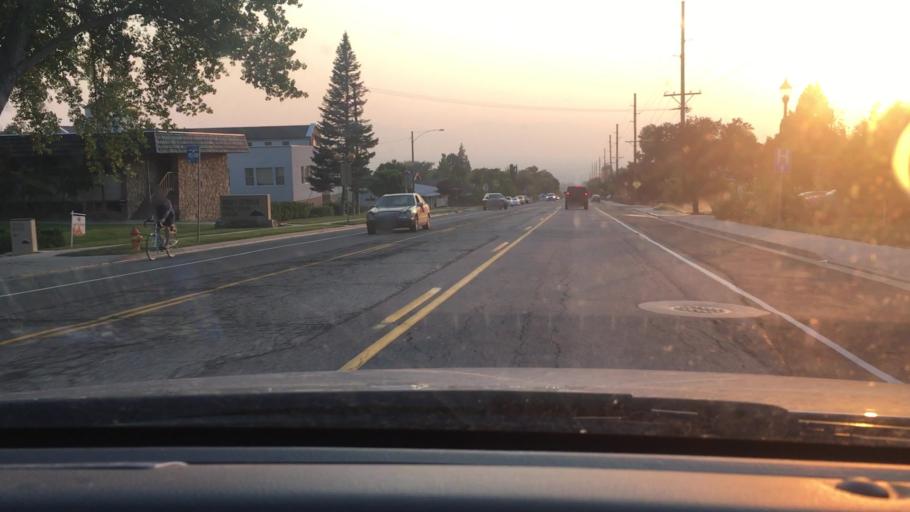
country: US
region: Utah
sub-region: Salt Lake County
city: Mount Olympus
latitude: 40.6870
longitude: -111.8007
